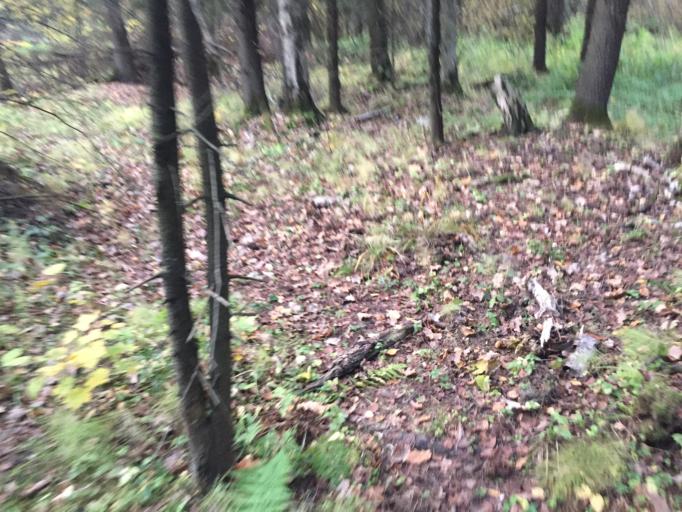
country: RU
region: Moscow
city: Gol'yanovo
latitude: 55.8562
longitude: 37.7833
